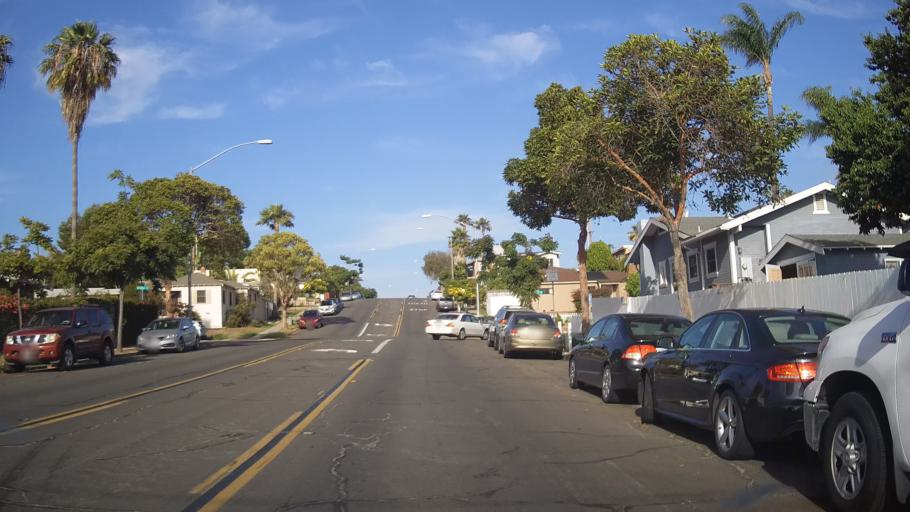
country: US
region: California
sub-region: San Diego County
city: San Diego
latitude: 32.7566
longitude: -117.1383
